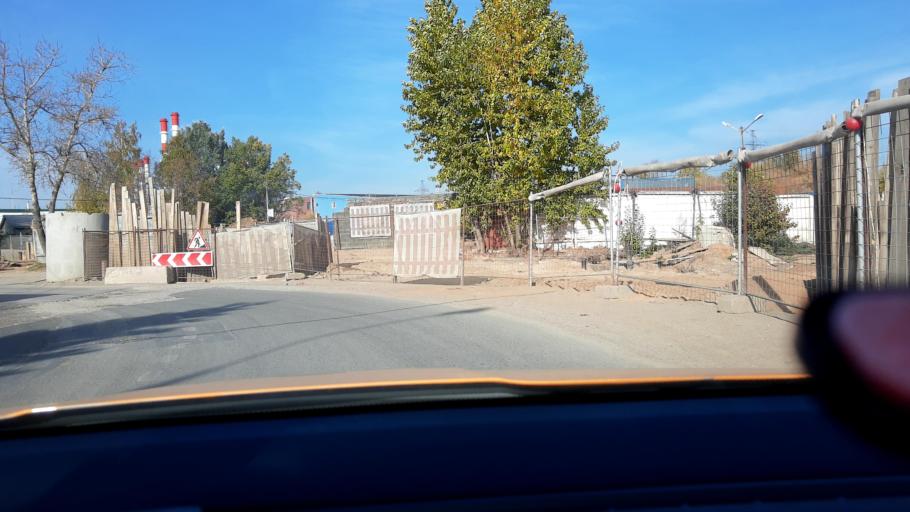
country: RU
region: Moscow
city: Tsaritsyno
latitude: 55.6444
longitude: 37.6426
